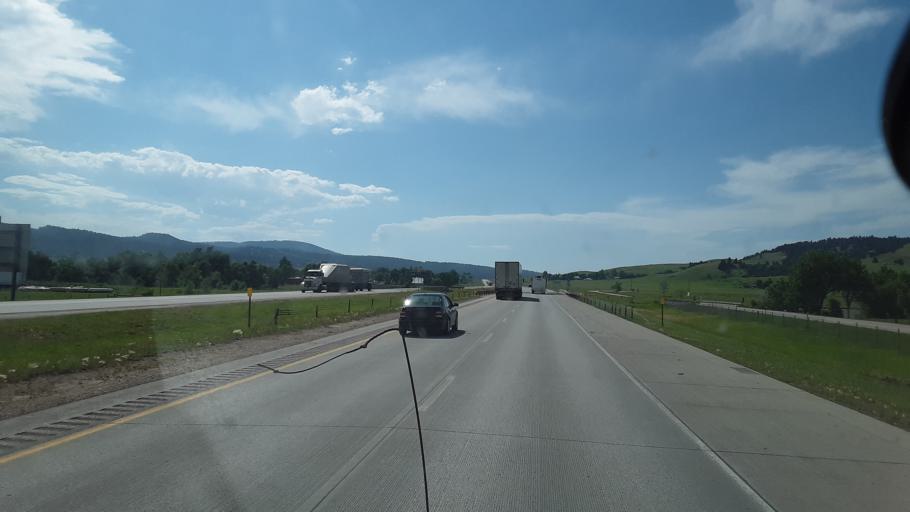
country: US
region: South Dakota
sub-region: Meade County
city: Sturgis
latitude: 44.4210
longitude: -103.5381
